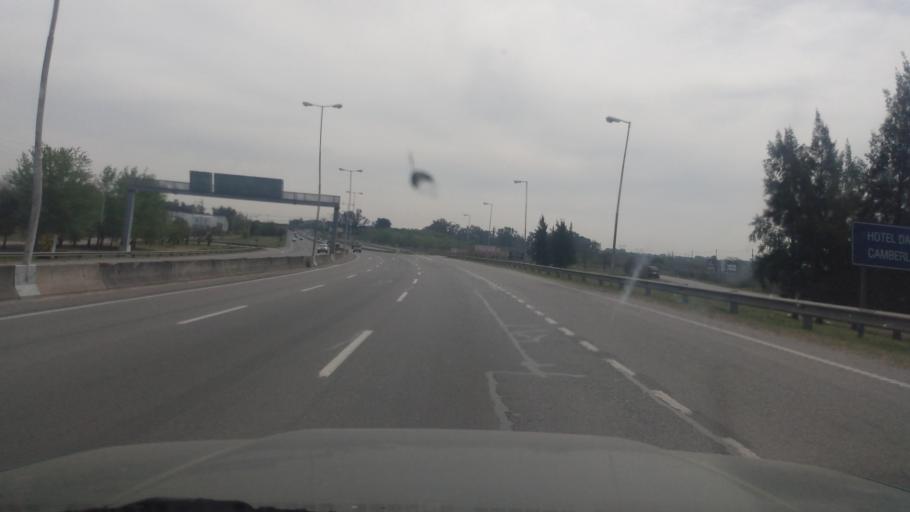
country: AR
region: Buenos Aires
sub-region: Partido de Pilar
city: Pilar
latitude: -34.4121
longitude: -59.0044
